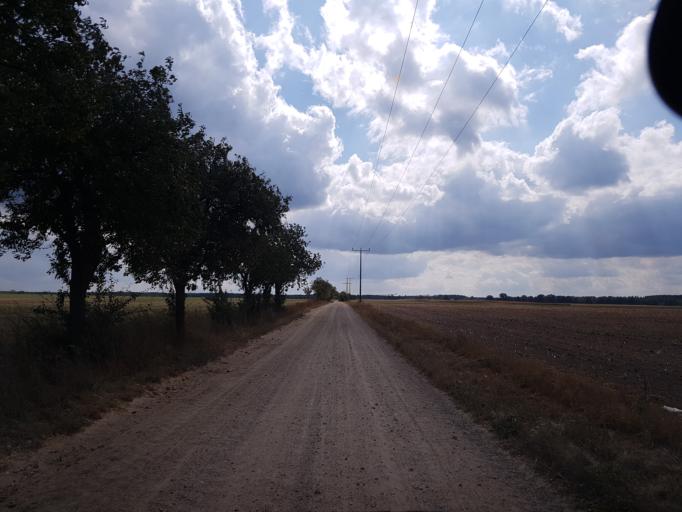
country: DE
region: Brandenburg
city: Finsterwalde
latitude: 51.6300
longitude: 13.7518
